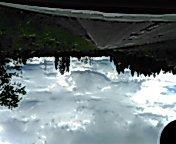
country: RU
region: Moskovskaya
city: Klin
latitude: 56.2583
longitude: 36.8373
